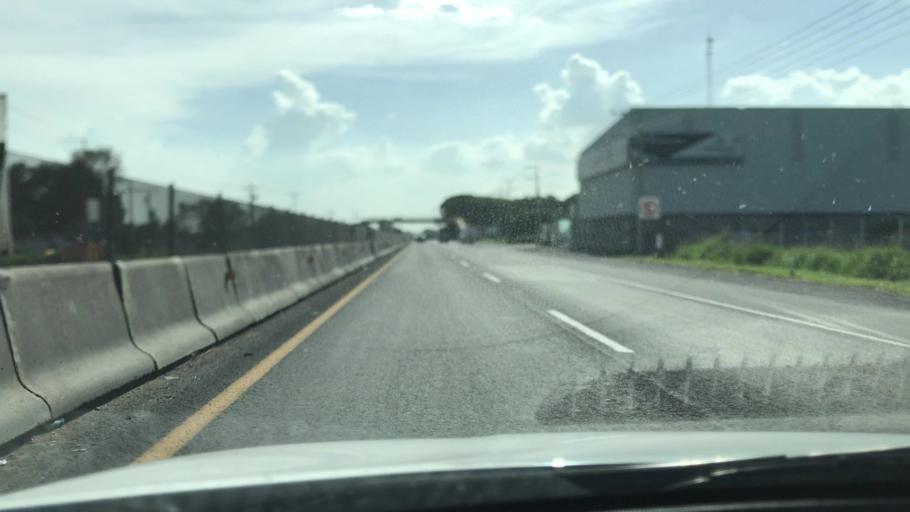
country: MX
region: Guanajuato
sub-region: Villagran
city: El Chinaco (El Pujido)
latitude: 20.5137
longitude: -100.9193
